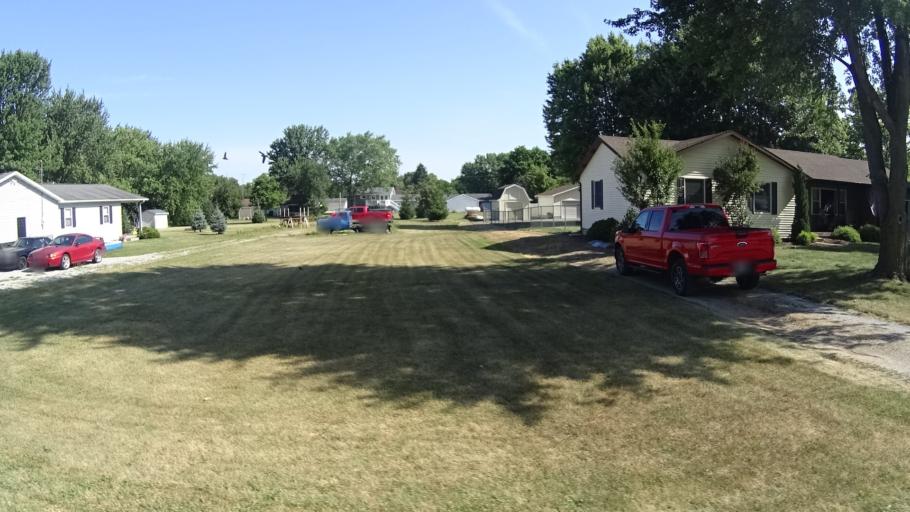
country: US
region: Ohio
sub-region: Huron County
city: Bellevue
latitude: 41.3704
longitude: -82.7963
